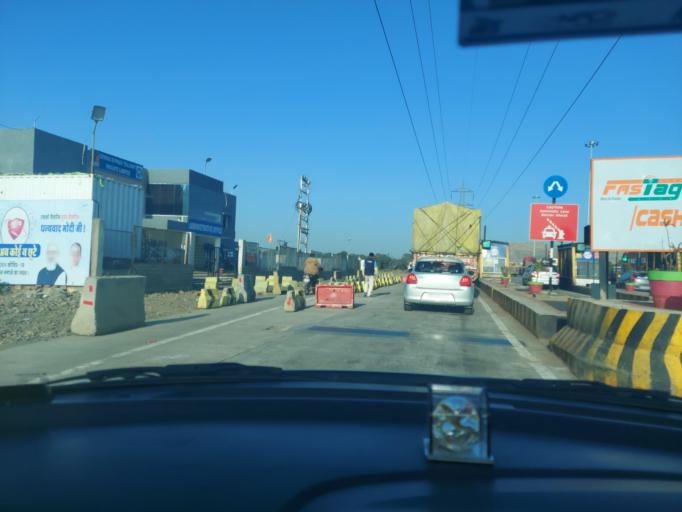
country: IN
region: Madhya Pradesh
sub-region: Dewas
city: Dewas
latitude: 22.9286
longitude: 76.0450
